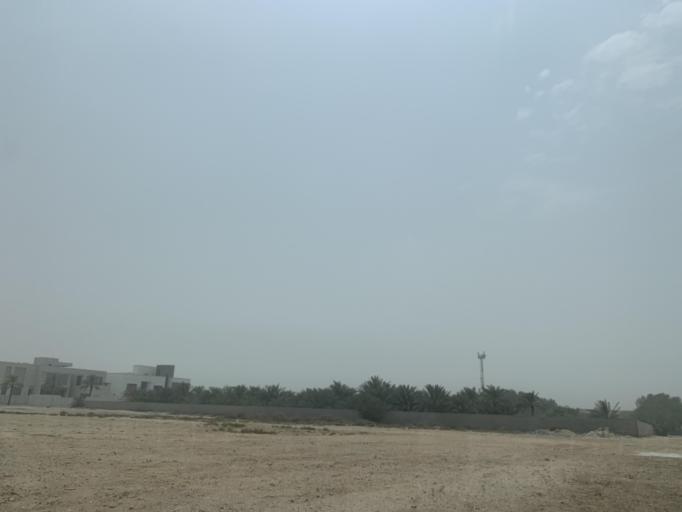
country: BH
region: Central Governorate
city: Madinat Hamad
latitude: 26.1648
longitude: 50.4748
